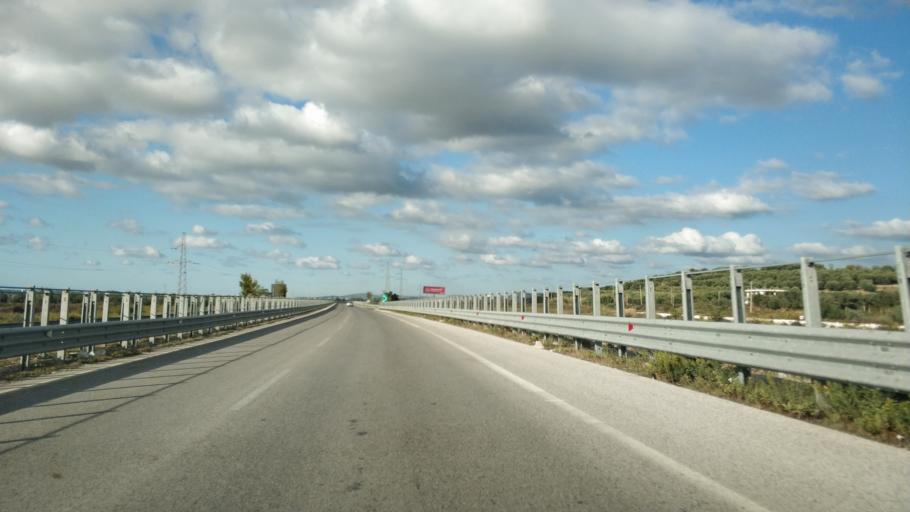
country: AL
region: Vlore
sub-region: Rrethi i Vlores
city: Novosele
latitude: 40.5661
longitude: 19.4704
